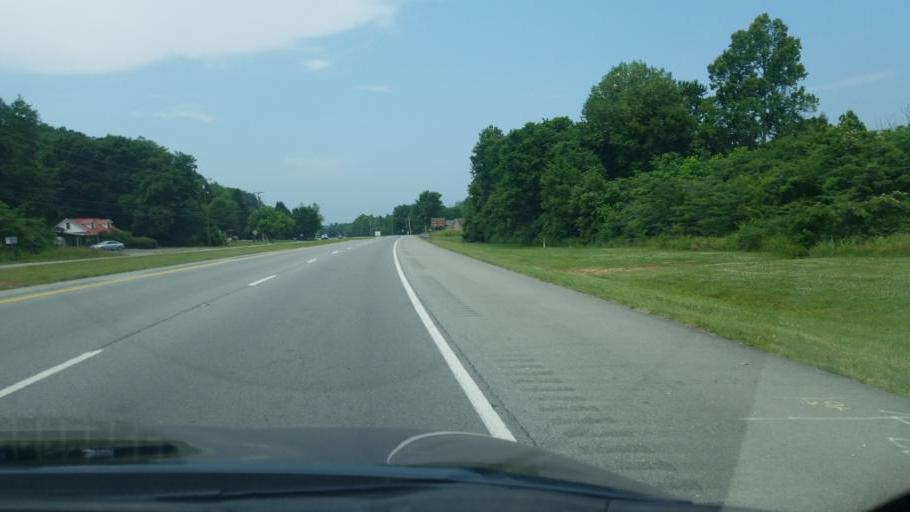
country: US
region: Tennessee
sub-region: Humphreys County
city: Waverly
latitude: 36.0794
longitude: -87.8382
